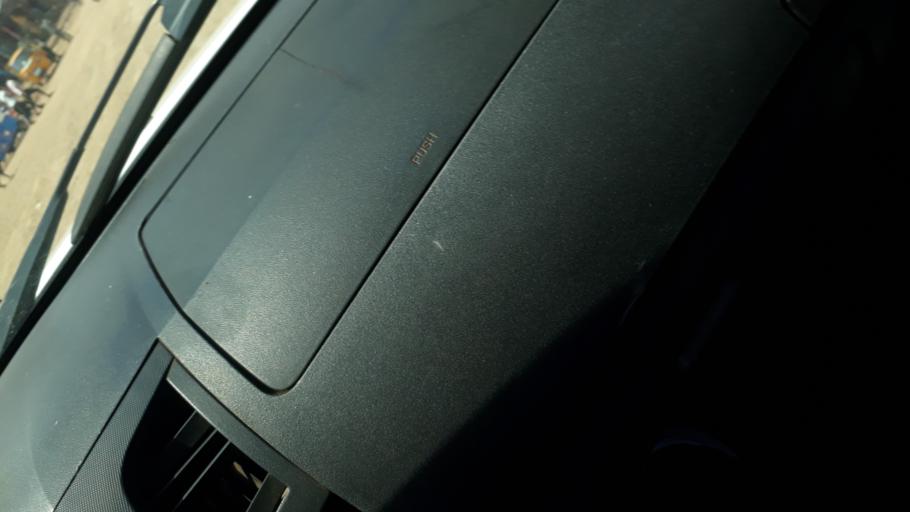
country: ET
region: Oromiya
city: Agaro
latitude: 7.8552
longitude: 36.5852
